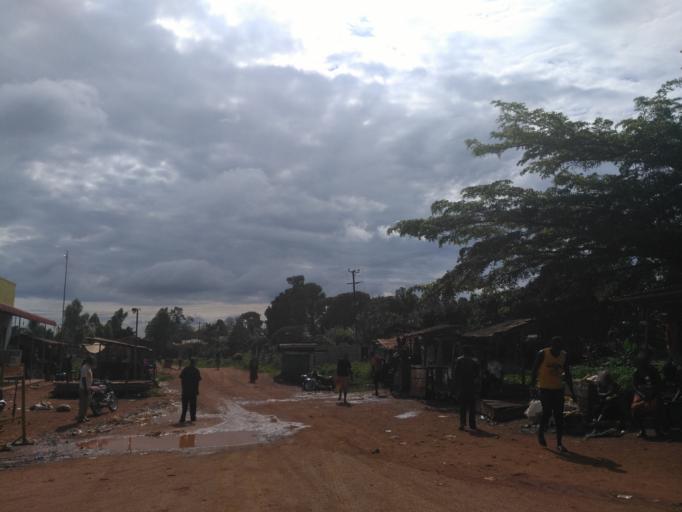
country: UG
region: Central Region
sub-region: Buikwe District
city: Njeru
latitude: 0.3959
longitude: 33.1738
